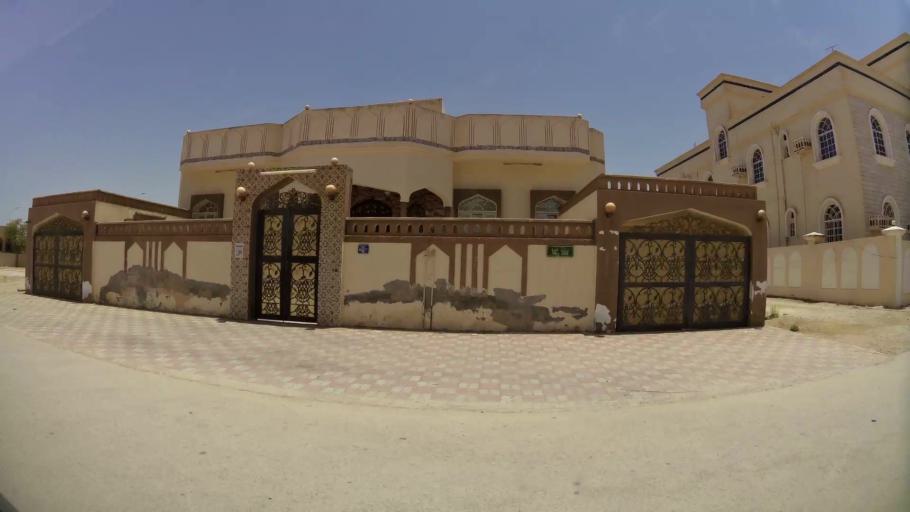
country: OM
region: Zufar
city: Salalah
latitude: 17.0754
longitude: 54.1583
